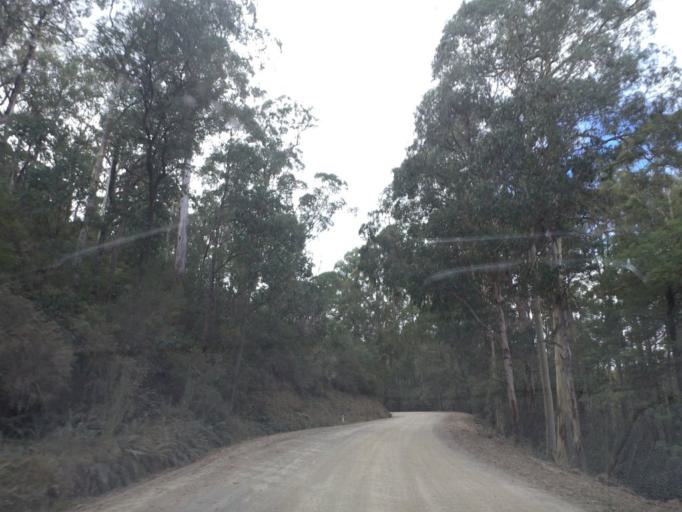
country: AU
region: Victoria
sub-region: Yarra Ranges
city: Millgrove
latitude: -37.5150
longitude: 145.9531
